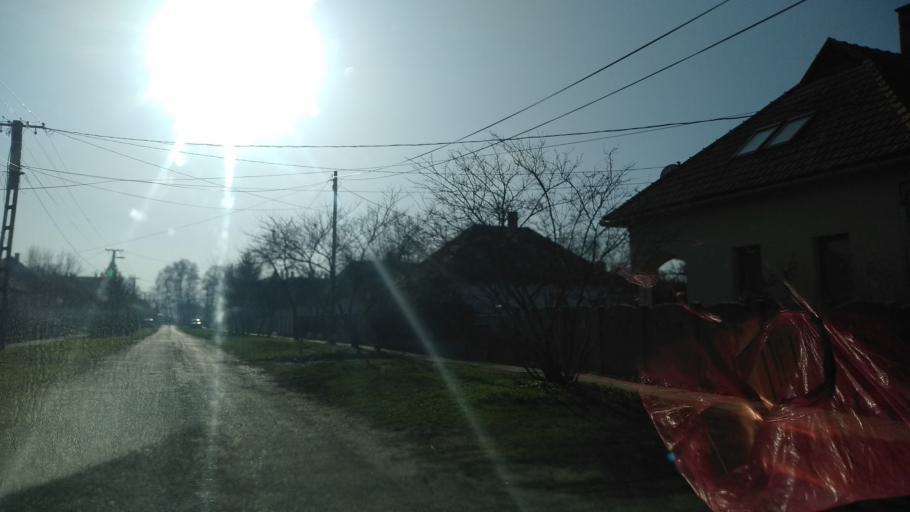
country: HU
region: Somogy
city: Barcs
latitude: 45.9648
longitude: 17.4896
